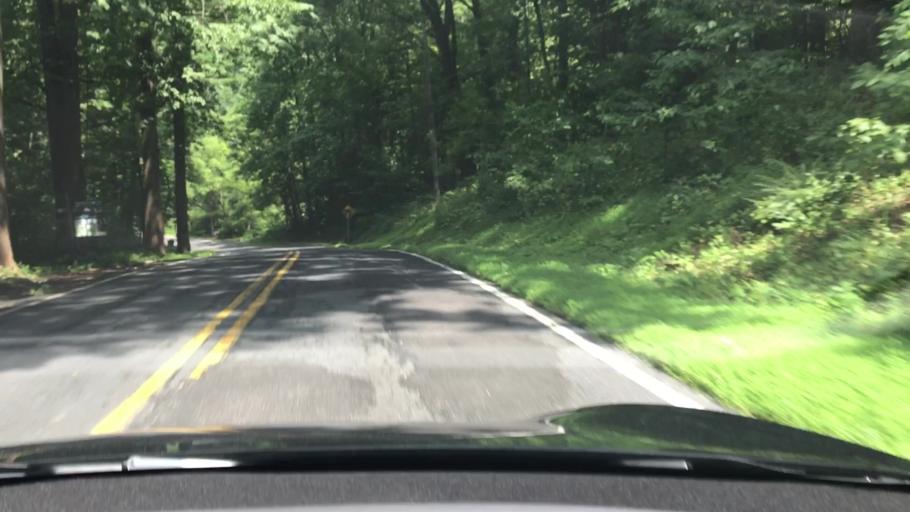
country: US
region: Pennsylvania
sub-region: Cumberland County
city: New Cumberland
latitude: 40.1883
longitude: -76.8722
